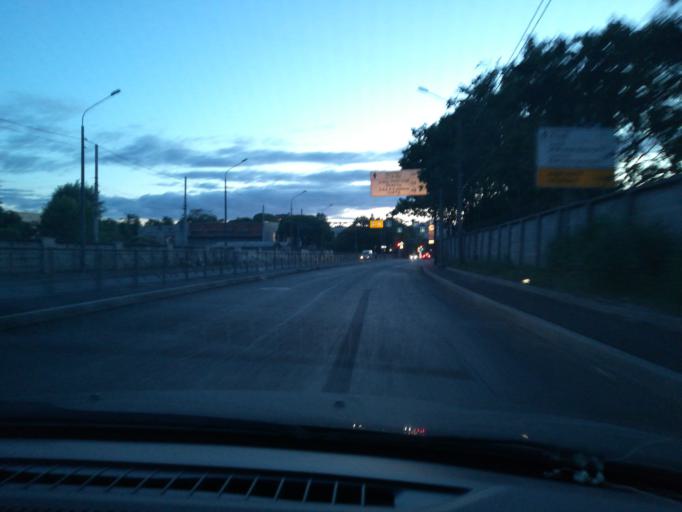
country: RU
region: St.-Petersburg
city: Avtovo
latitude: 59.8587
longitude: 30.2603
